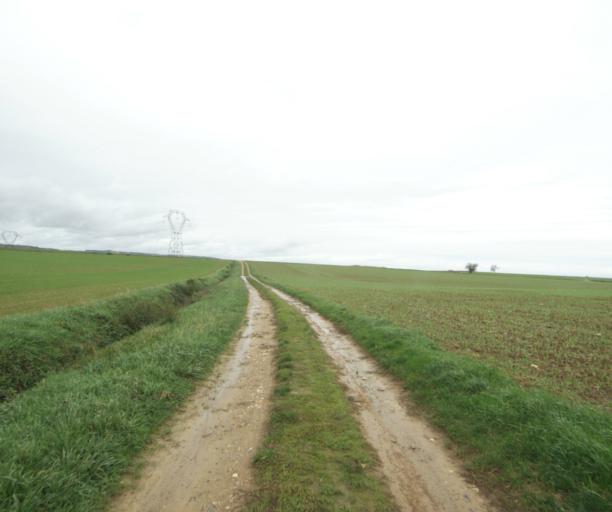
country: FR
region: Bourgogne
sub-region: Departement de Saone-et-Loire
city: Saint-Martin-Belle-Roche
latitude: 46.4664
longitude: 4.8562
